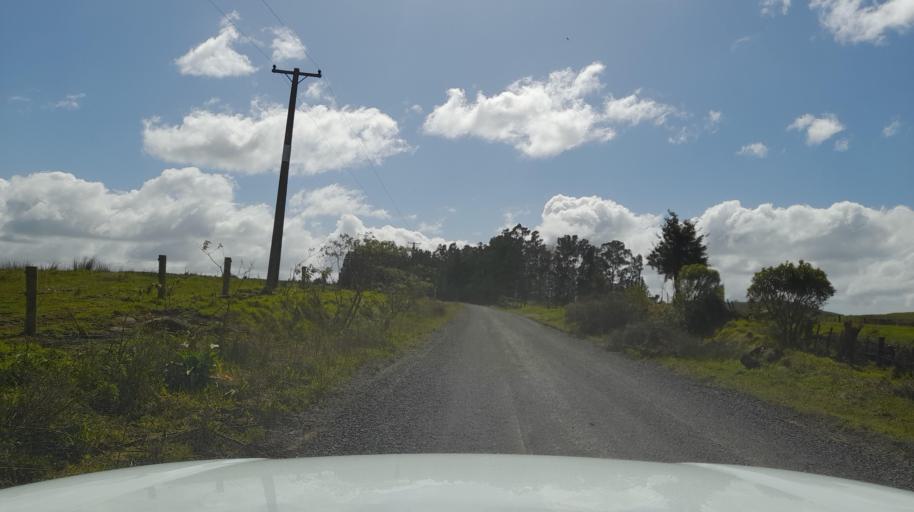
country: NZ
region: Northland
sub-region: Far North District
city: Kerikeri
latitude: -35.2273
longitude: 173.8759
